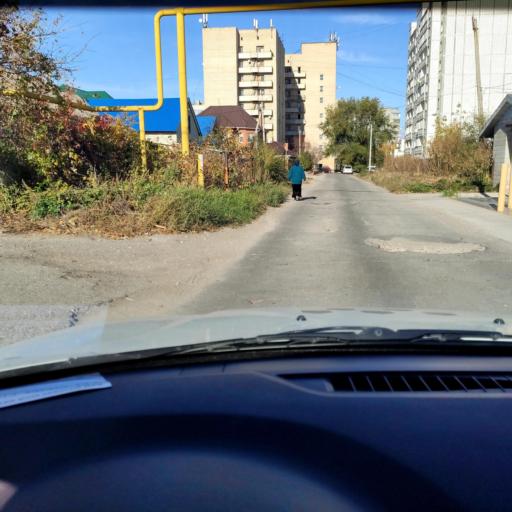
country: RU
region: Samara
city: Tol'yatti
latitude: 53.5378
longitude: 49.4062
